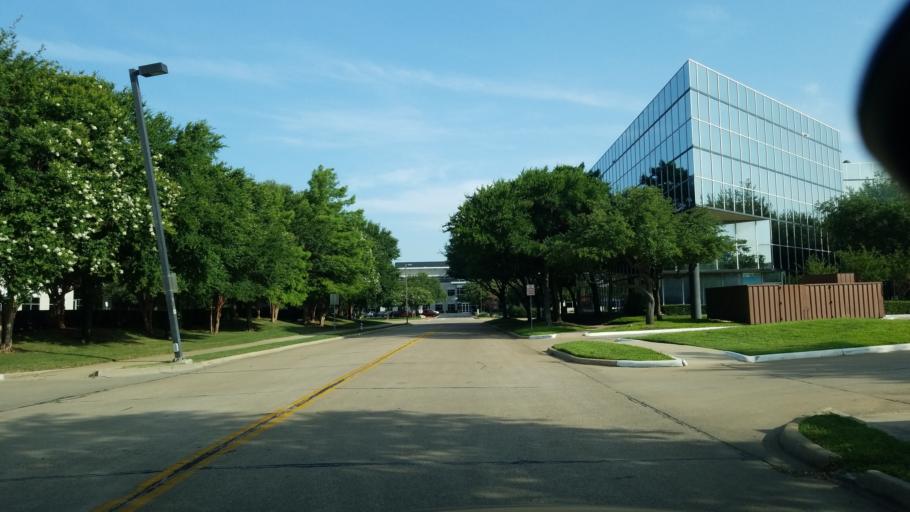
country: US
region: Texas
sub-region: Dallas County
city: Coppell
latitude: 32.9234
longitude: -97.0140
